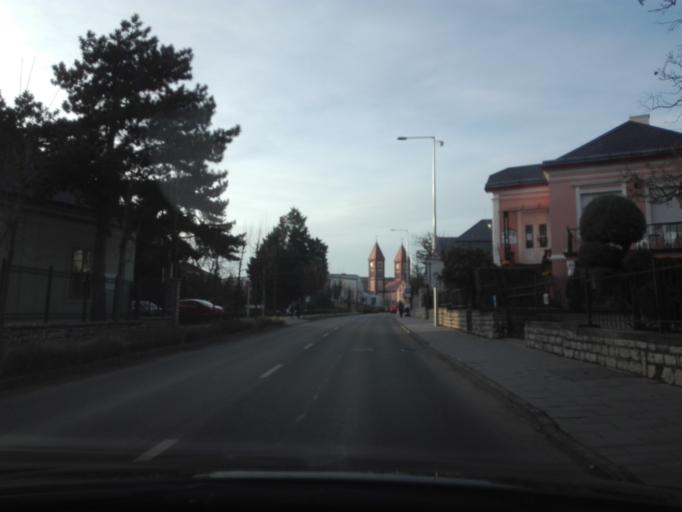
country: HU
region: Veszprem
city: Balatonfured
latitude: 46.9607
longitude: 17.8780
